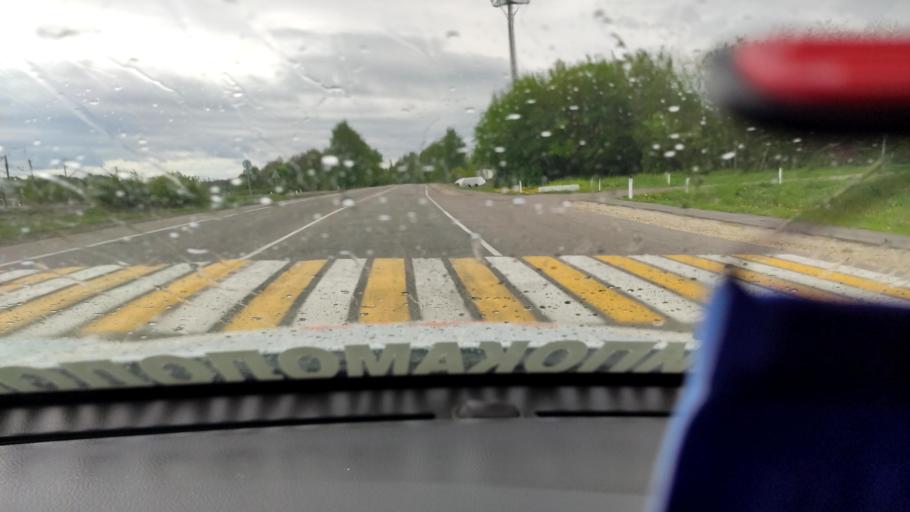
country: RU
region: Voronezj
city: Imeni Pervogo Maya
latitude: 50.7512
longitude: 39.3880
